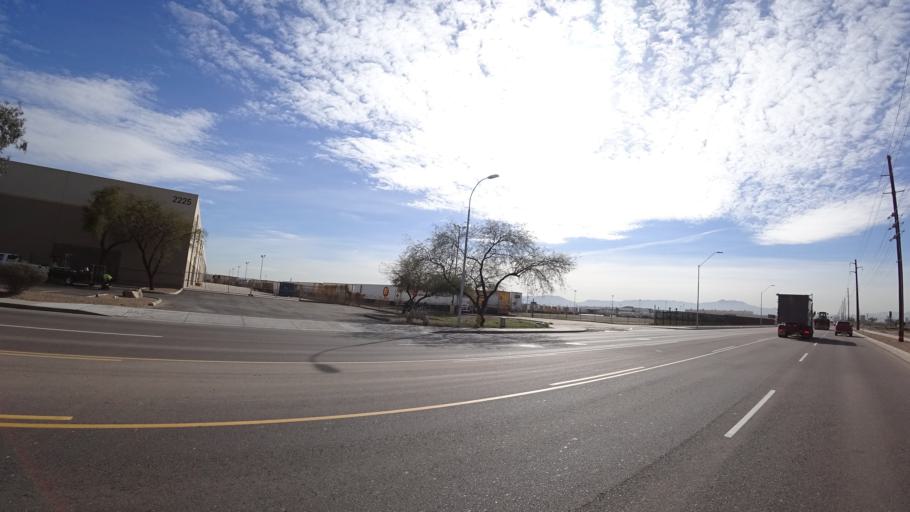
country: US
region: Arizona
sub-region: Maricopa County
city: Laveen
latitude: 33.4263
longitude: -112.1518
